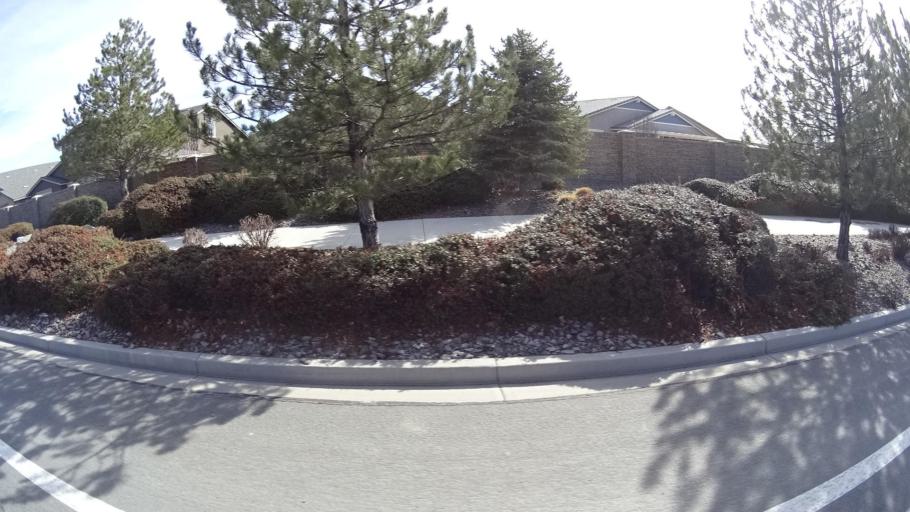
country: US
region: Nevada
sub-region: Washoe County
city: Sun Valley
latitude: 39.6018
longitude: -119.7288
